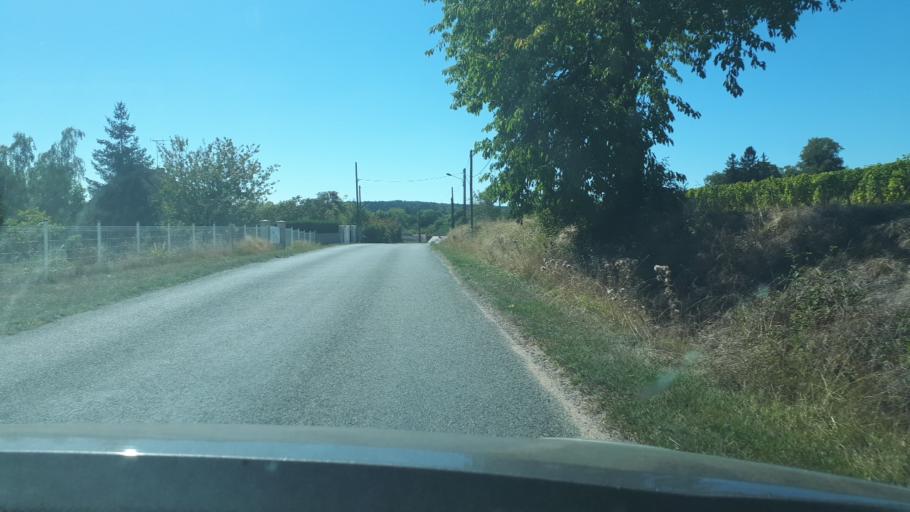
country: FR
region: Centre
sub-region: Departement du Cher
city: Sancerre
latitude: 47.2622
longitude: 2.7640
